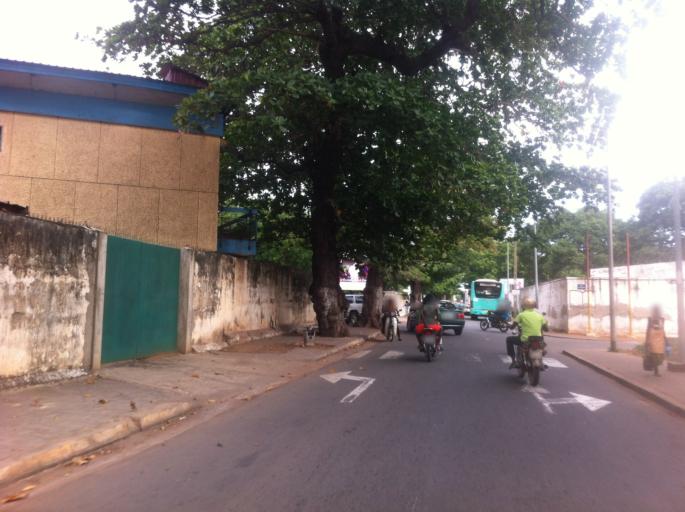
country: TG
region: Maritime
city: Lome
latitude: 6.1299
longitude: 1.2185
